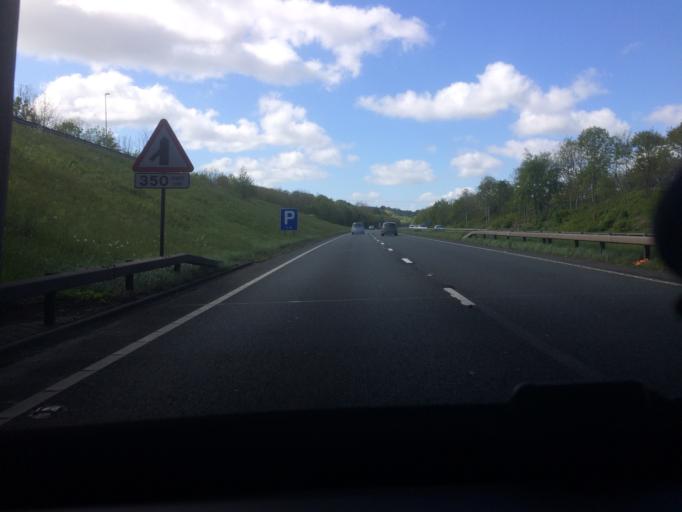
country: GB
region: Wales
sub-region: Wrexham
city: Rossett
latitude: 53.1056
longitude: -2.9574
